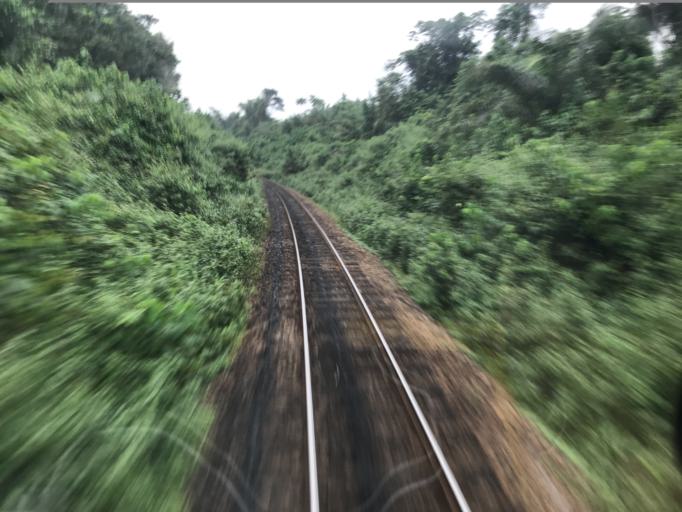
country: CM
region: Littoral
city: Edea
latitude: 3.9263
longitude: 10.1089
